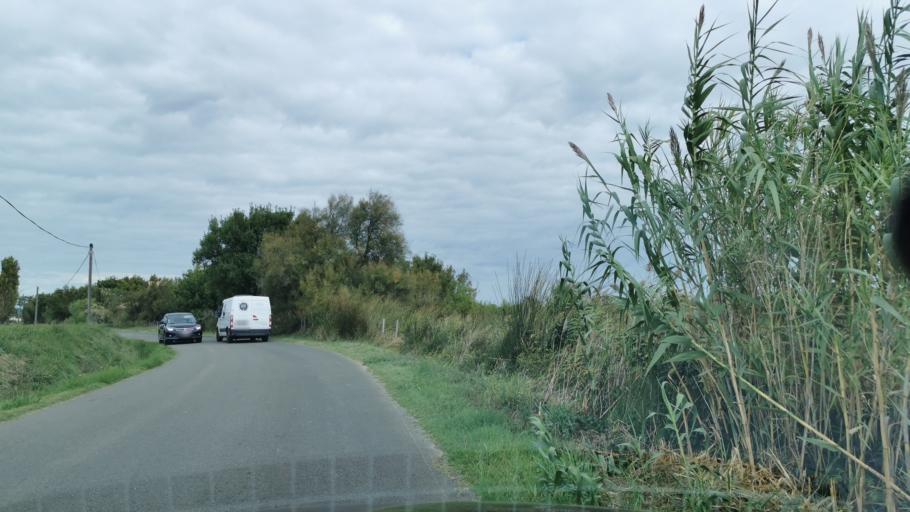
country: FR
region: Languedoc-Roussillon
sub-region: Departement de l'Herault
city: Lespignan
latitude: 43.2288
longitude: 3.1942
